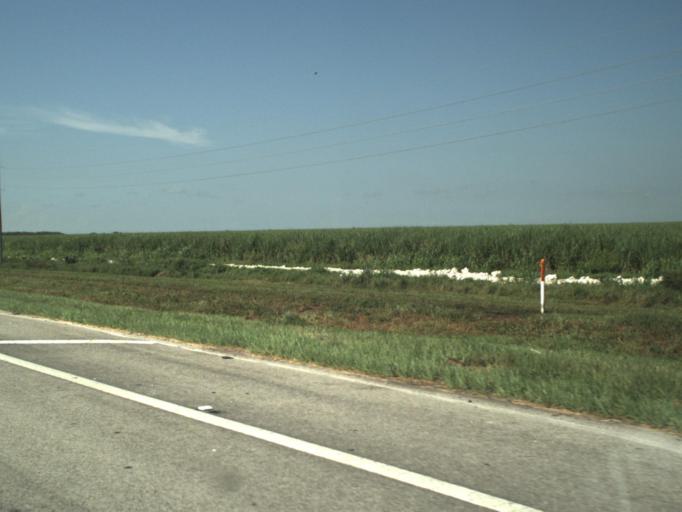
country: US
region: Florida
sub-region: Palm Beach County
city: Belle Glade Camp
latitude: 26.5771
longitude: -80.7110
